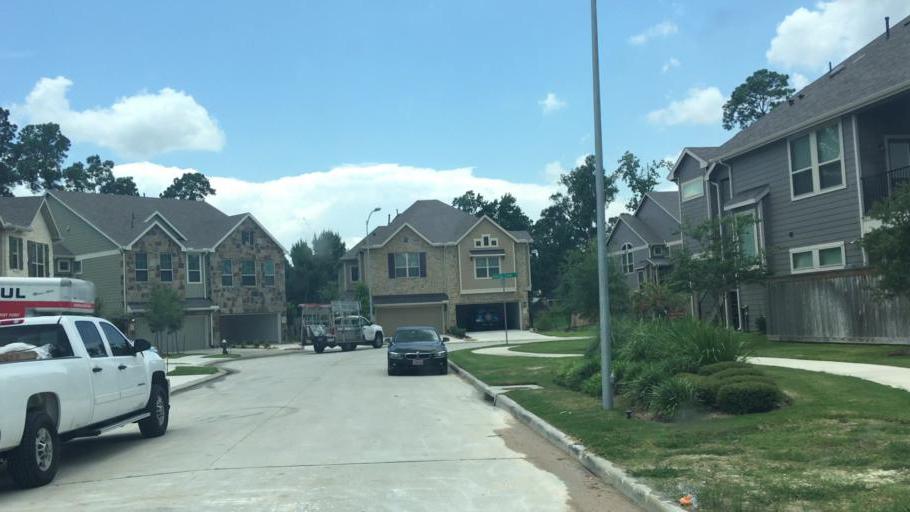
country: US
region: Texas
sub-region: Harris County
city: Atascocita
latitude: 29.9887
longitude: -95.1873
